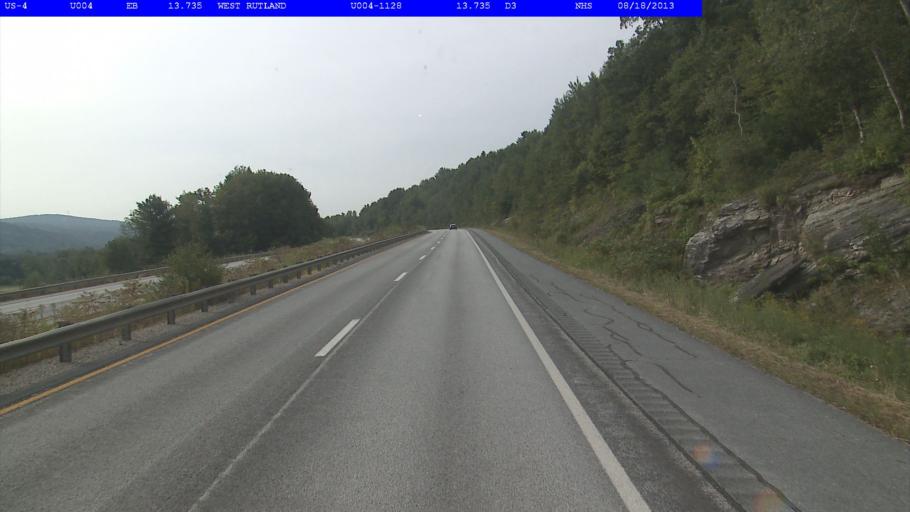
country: US
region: Vermont
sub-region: Rutland County
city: West Rutland
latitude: 43.5968
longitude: -73.0571
